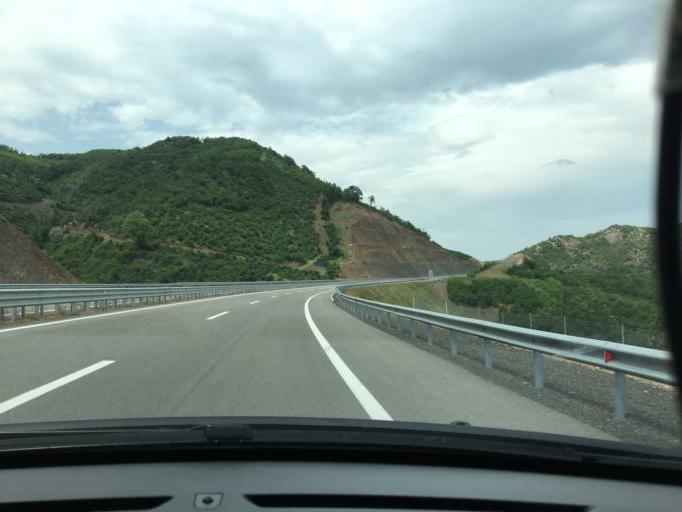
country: MK
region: Gevgelija
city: Miravci
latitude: 41.3526
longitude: 22.3610
